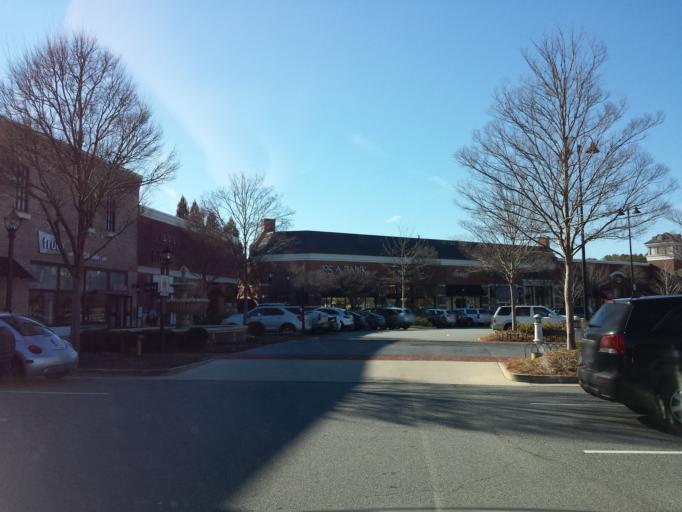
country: US
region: Georgia
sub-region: Cobb County
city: Kennesaw
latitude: 33.9516
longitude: -84.6574
